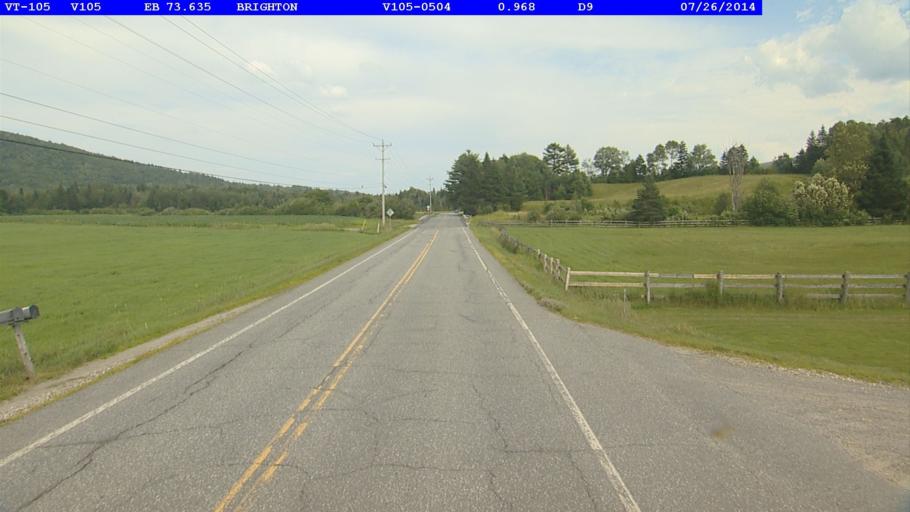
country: US
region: Vermont
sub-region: Caledonia County
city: Lyndonville
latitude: 44.8061
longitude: -71.9304
